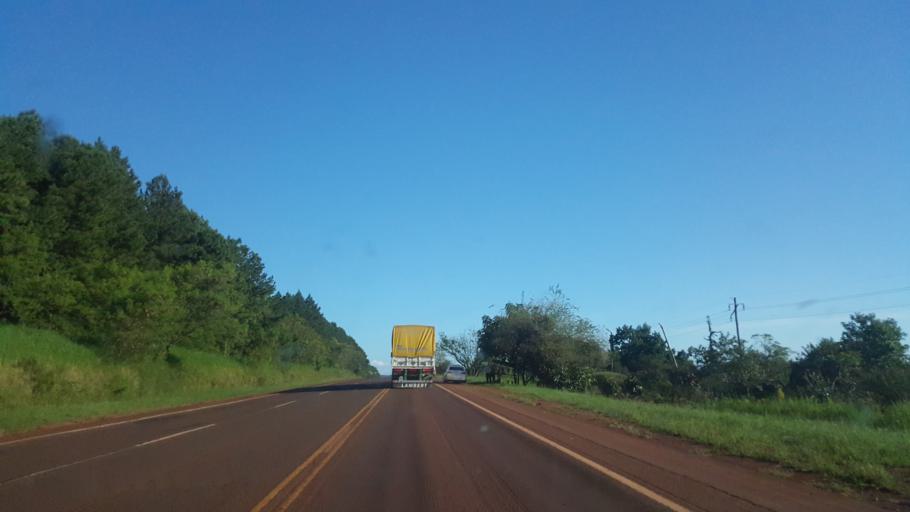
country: AR
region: Misiones
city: Puerto Esperanza
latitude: -26.1841
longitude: -54.5894
